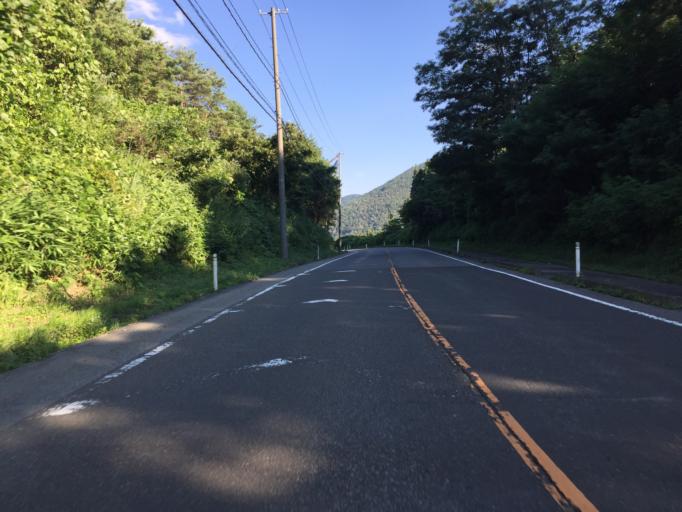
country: JP
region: Miyagi
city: Shiroishi
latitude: 37.9861
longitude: 140.4591
